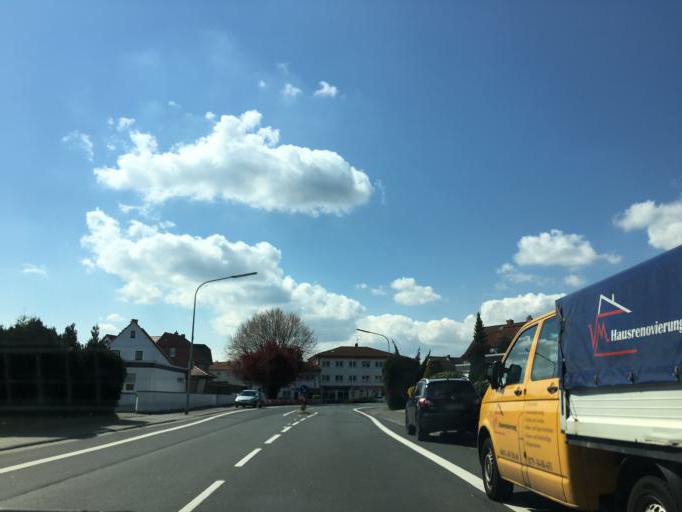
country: DE
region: Hesse
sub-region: Regierungsbezirk Darmstadt
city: Eppertshausen
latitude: 49.9812
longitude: 8.8230
